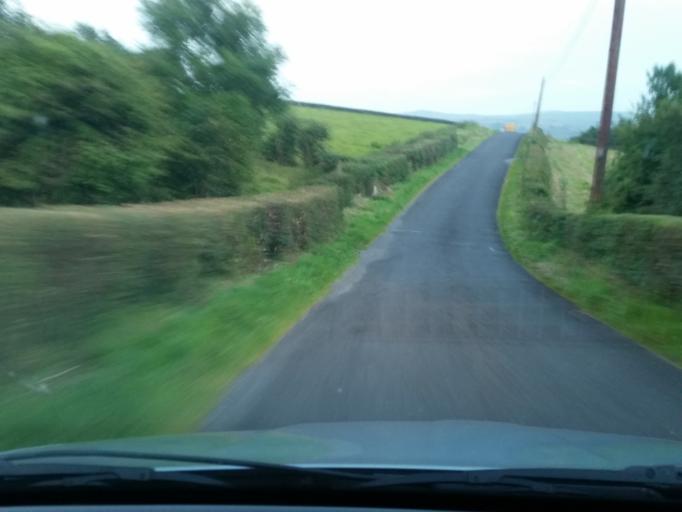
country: GB
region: Northern Ireland
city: Fivemiletown
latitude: 54.2972
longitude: -7.2864
